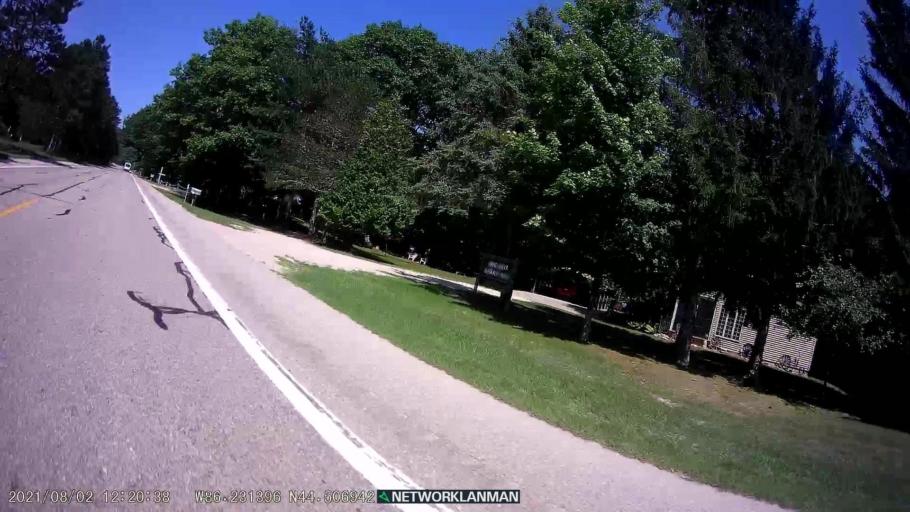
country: US
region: Michigan
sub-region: Benzie County
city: Frankfort
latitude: 44.5067
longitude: -86.2317
